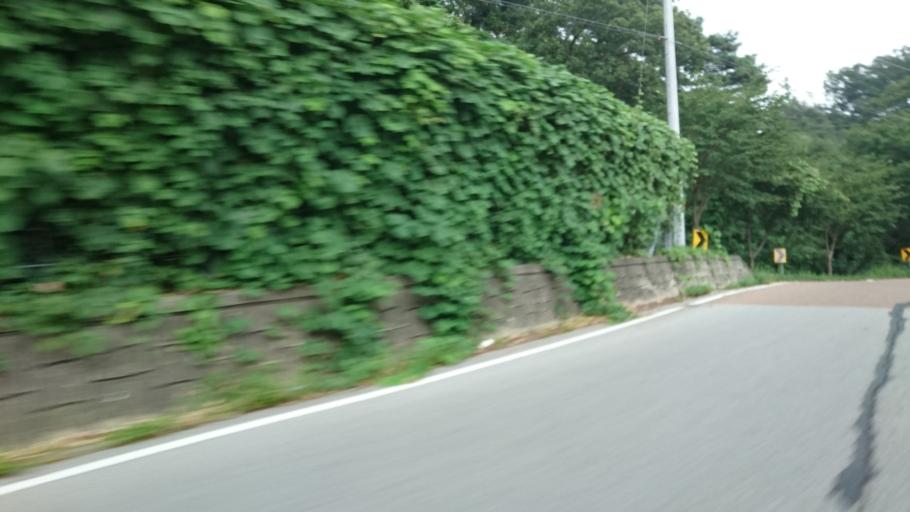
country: KR
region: Daegu
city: Daegu
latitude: 36.0219
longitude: 128.5640
